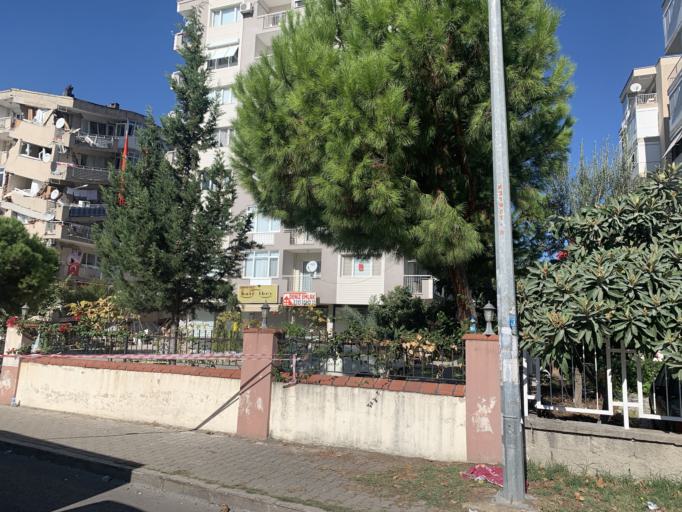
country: TR
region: Izmir
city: Bornova
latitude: 38.4630
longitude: 27.1902
